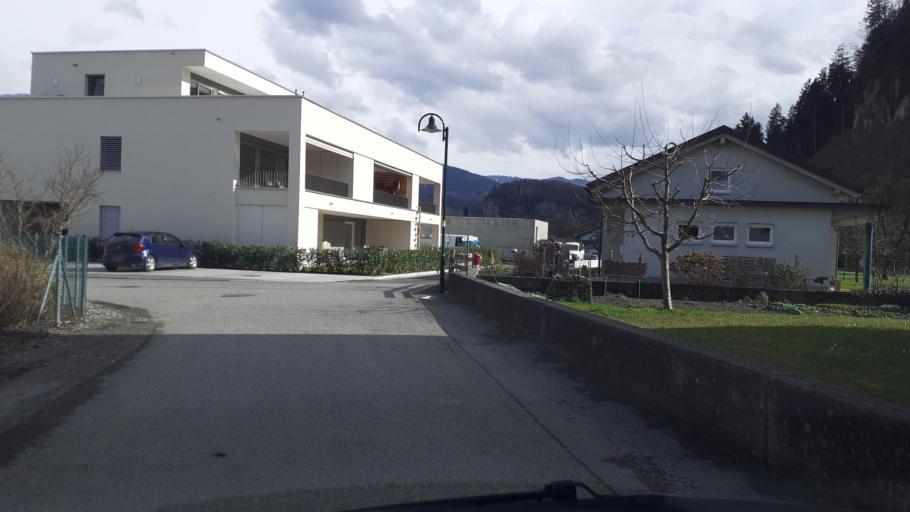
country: AT
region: Vorarlberg
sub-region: Politischer Bezirk Feldkirch
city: Mader
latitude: 47.3440
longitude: 9.6123
